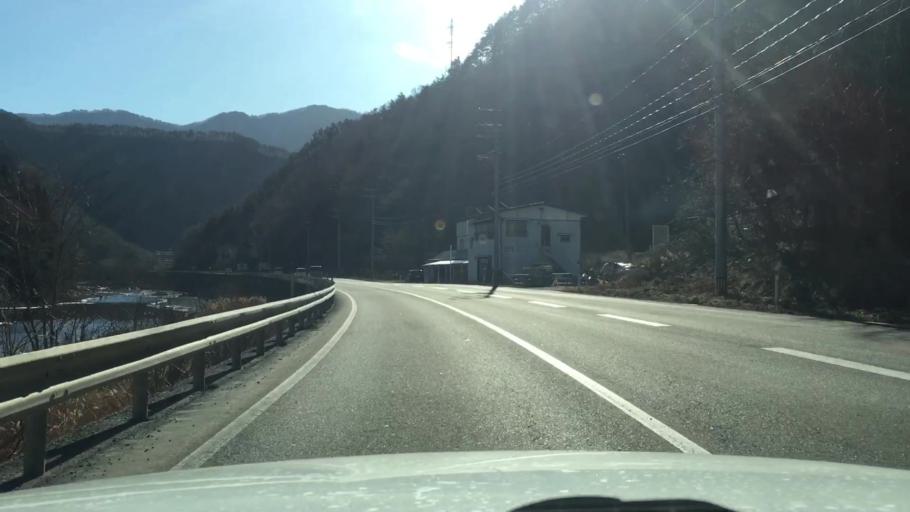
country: JP
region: Iwate
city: Miyako
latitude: 39.6155
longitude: 141.7890
